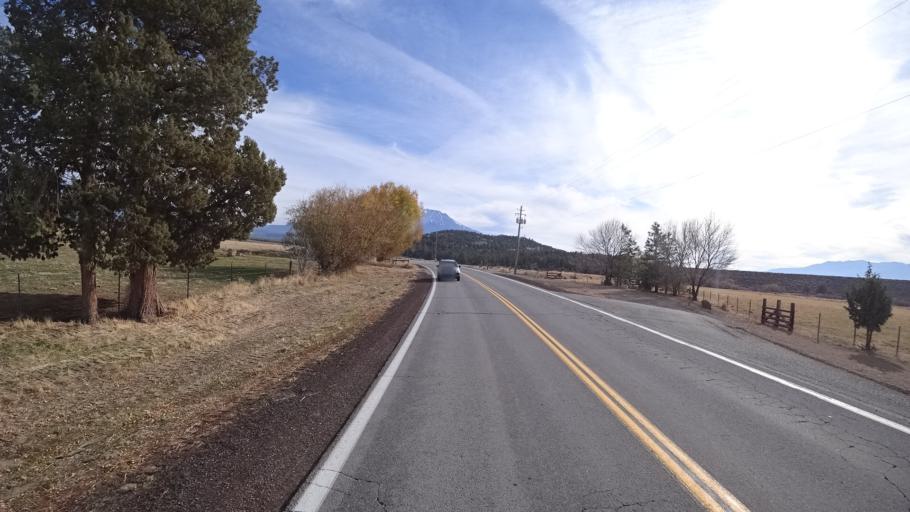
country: US
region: California
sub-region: Siskiyou County
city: Weed
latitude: 41.5457
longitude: -122.3742
